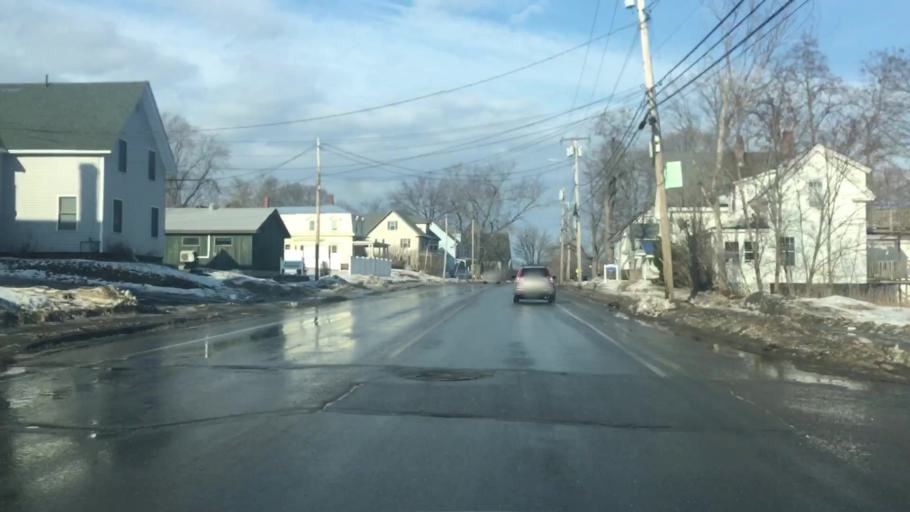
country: US
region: Maine
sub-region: Penobscot County
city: Bangor
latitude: 44.7748
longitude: -68.7793
